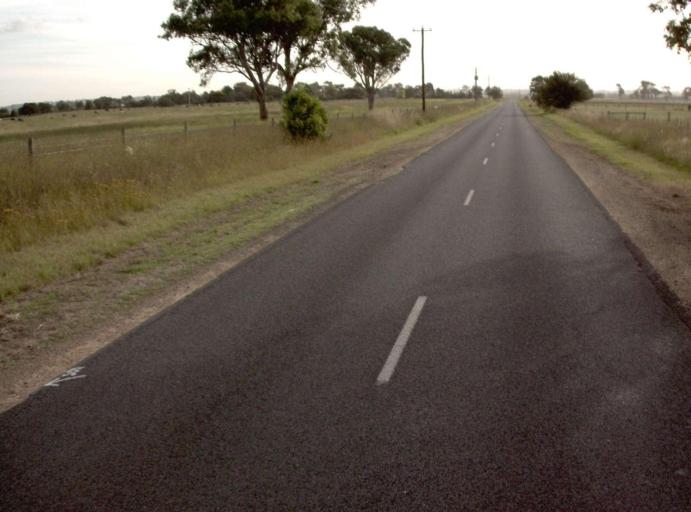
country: AU
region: Victoria
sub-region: Wellington
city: Sale
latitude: -37.8612
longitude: 147.0355
